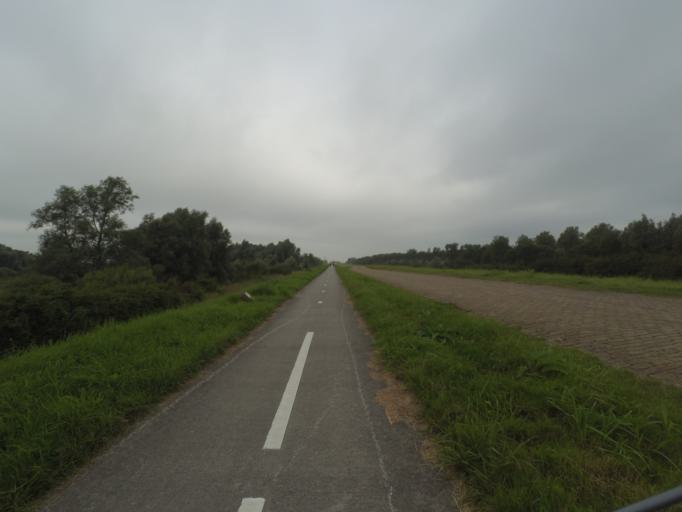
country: NL
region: Flevoland
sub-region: Gemeente Lelystad
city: Lelystad
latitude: 52.4484
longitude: 5.4322
